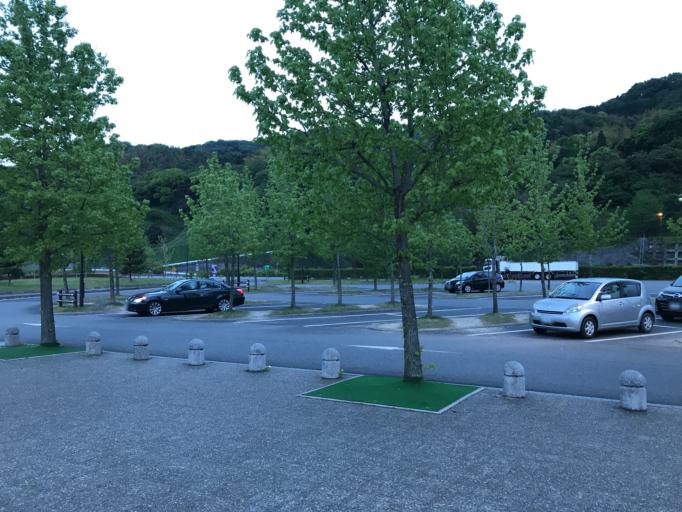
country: JP
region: Ehime
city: Masaki-cho
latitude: 33.7708
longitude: 132.7531
